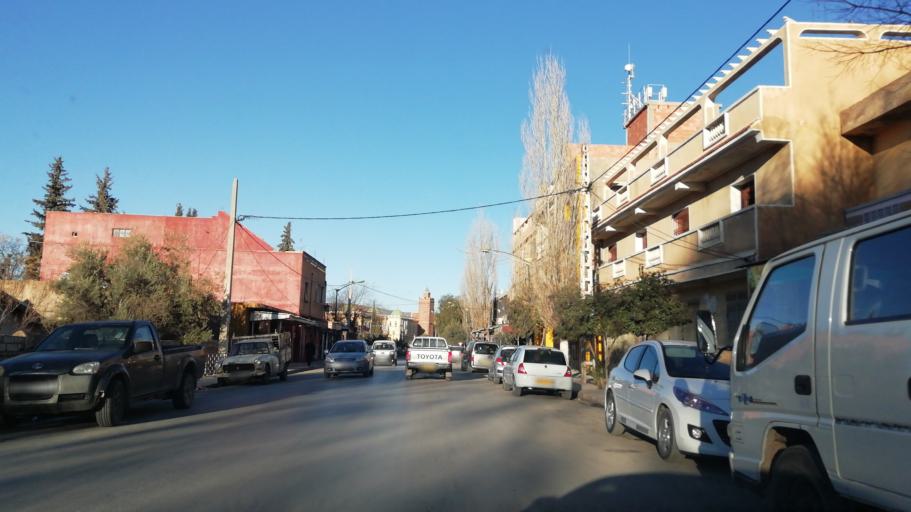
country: DZ
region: Tlemcen
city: Sebdou
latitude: 34.6430
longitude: -1.3271
